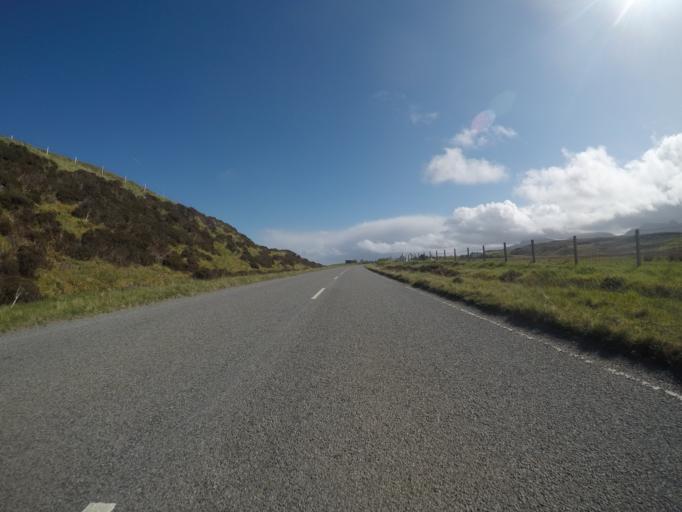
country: GB
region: Scotland
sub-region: Highland
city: Portree
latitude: 57.6001
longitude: -6.1644
